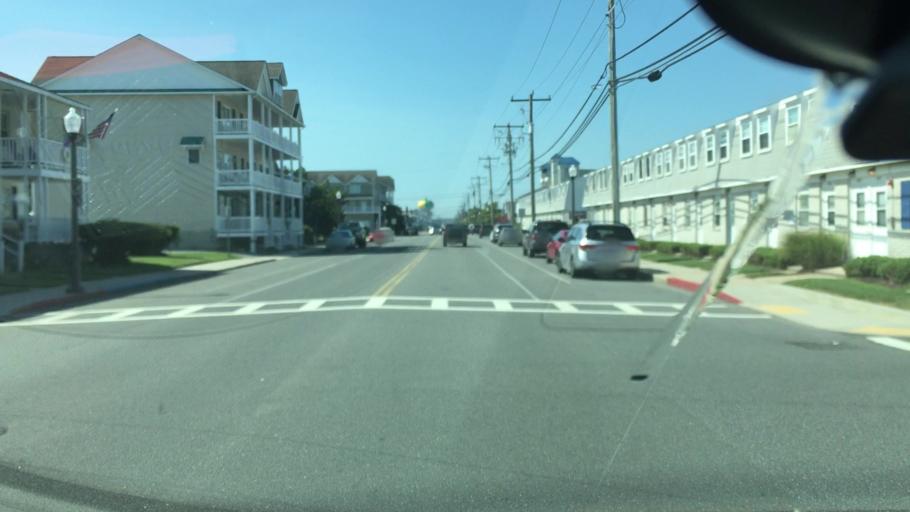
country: US
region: Maryland
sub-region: Worcester County
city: Ocean City
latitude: 38.3441
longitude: -75.0822
